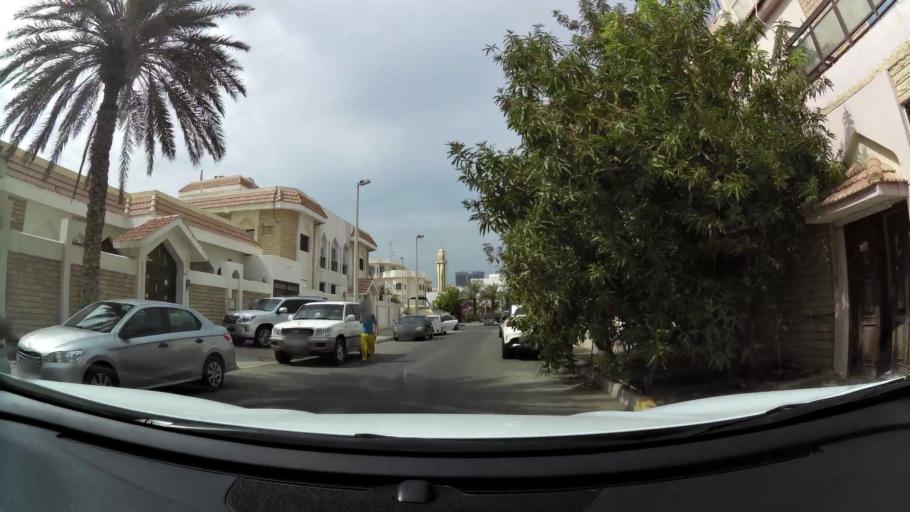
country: AE
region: Abu Dhabi
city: Abu Dhabi
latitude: 24.4690
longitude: 54.3617
